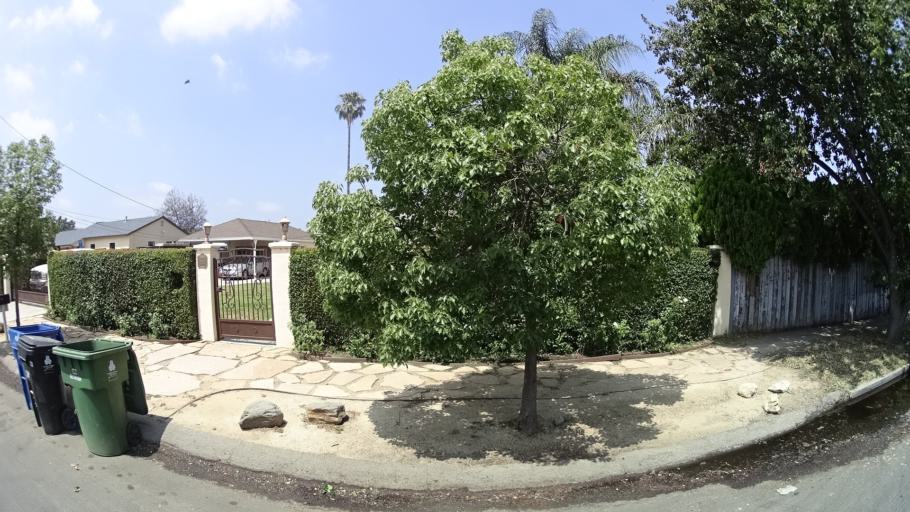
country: US
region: California
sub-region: Los Angeles County
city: Van Nuys
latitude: 34.1900
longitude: -118.4641
